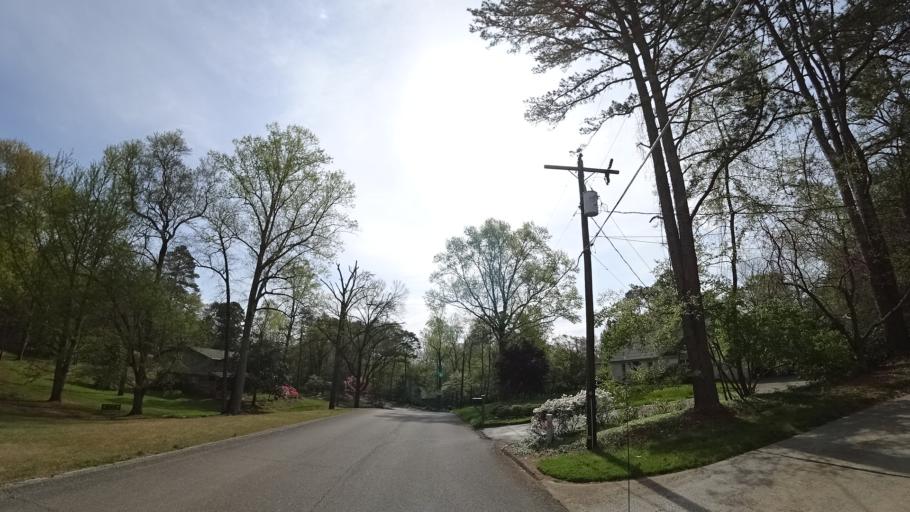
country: US
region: Tennessee
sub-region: Knox County
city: Knoxville
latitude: 35.8999
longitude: -83.9779
